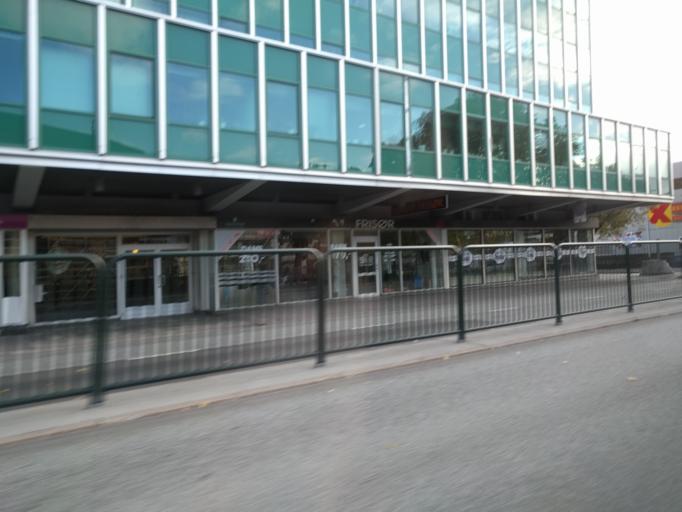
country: NO
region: Vest-Agder
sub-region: Kristiansand
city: Kristiansand
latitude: 58.1465
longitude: 7.9876
